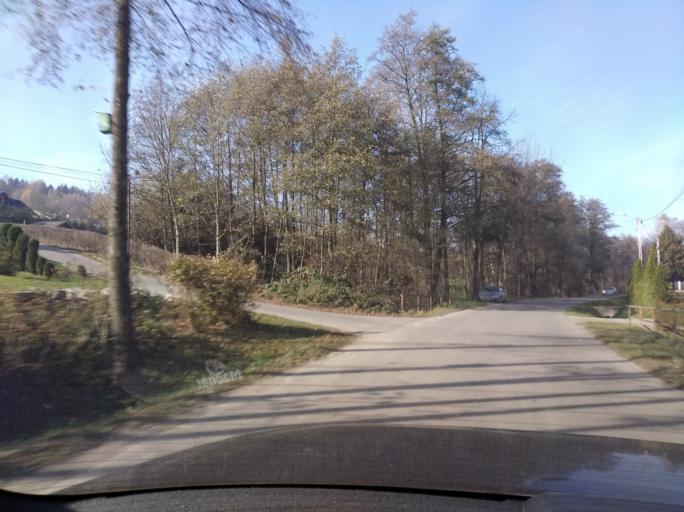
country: PL
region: Subcarpathian Voivodeship
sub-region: Powiat strzyzowski
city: Frysztak
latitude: 49.8821
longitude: 21.6094
